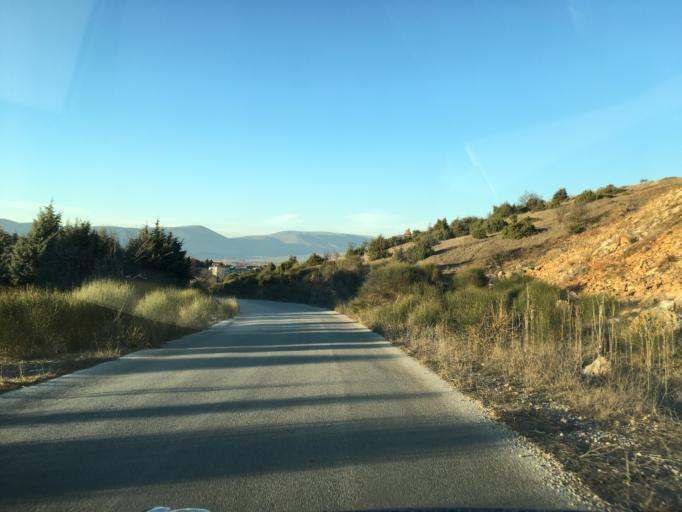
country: GR
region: West Macedonia
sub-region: Nomos Kozanis
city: Kozani
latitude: 40.2807
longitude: 21.7332
